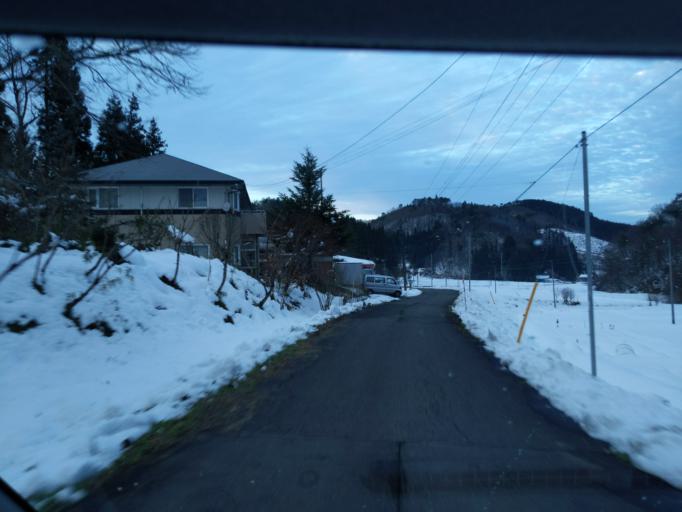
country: JP
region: Iwate
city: Mizusawa
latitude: 39.0435
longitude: 141.0116
